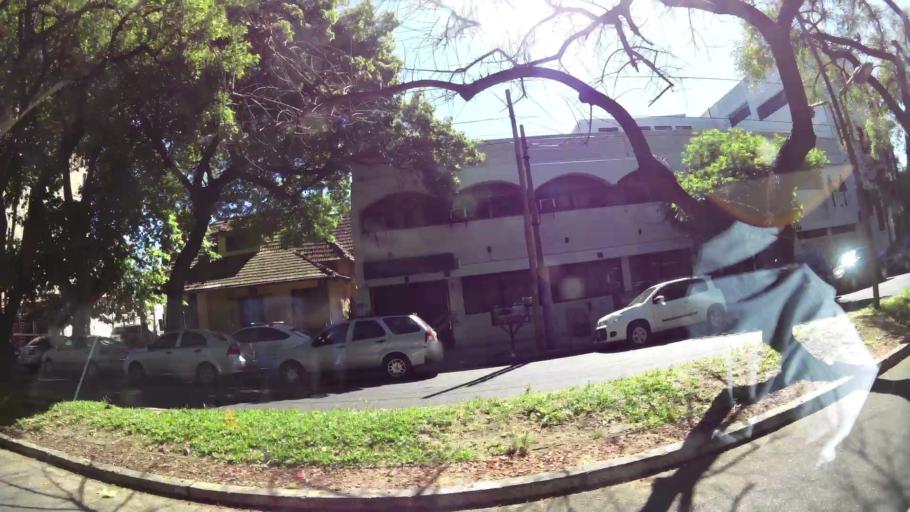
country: AR
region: Buenos Aires
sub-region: Partido de General San Martin
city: General San Martin
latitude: -34.5718
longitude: -58.5371
